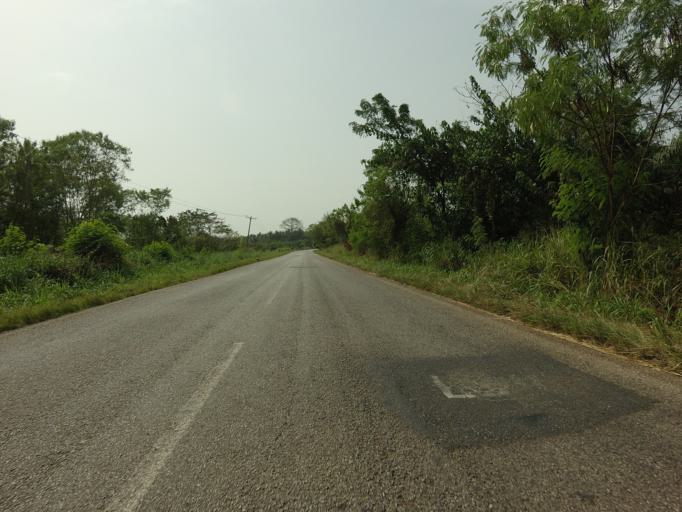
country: GH
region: Volta
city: Ho
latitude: 6.3233
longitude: 0.1631
